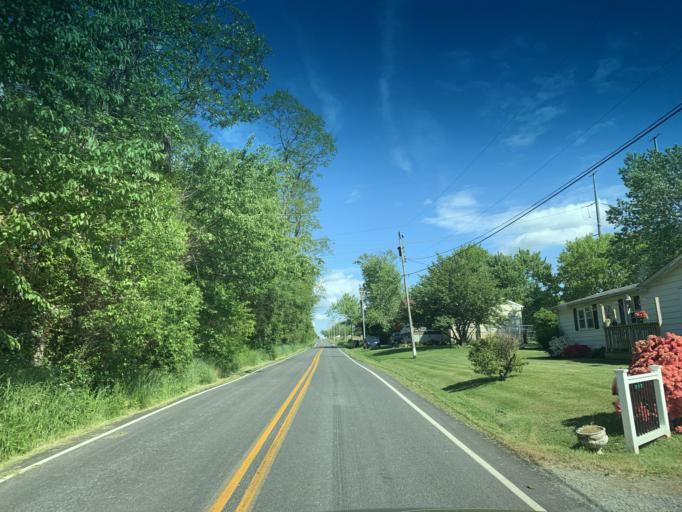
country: US
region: Maryland
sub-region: Cecil County
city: Rising Sun
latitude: 39.7177
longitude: -76.1641
